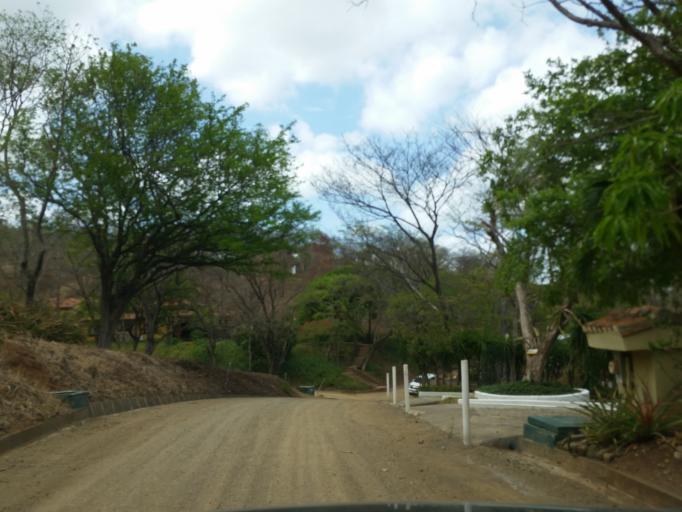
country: NI
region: Rivas
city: Tola
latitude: 11.4361
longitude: -86.0835
